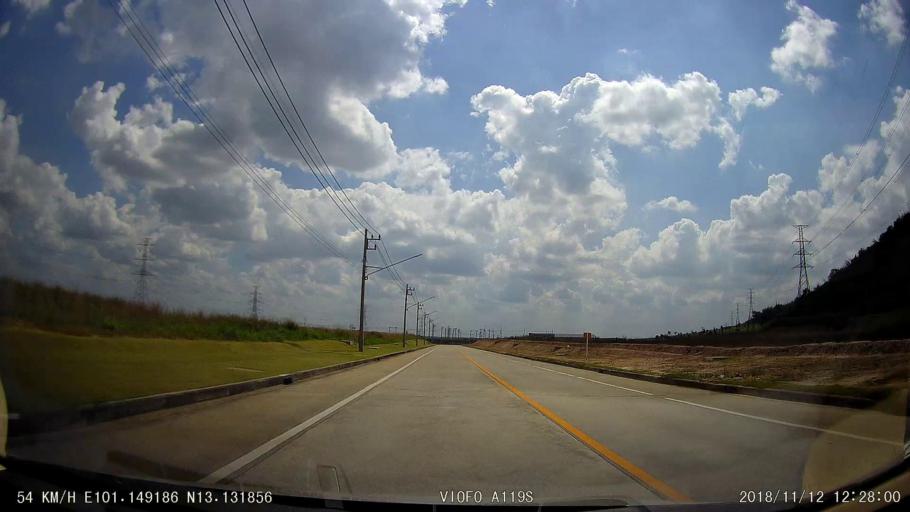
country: TH
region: Chon Buri
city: Ban Talat Bueng
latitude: 13.1316
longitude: 101.1492
